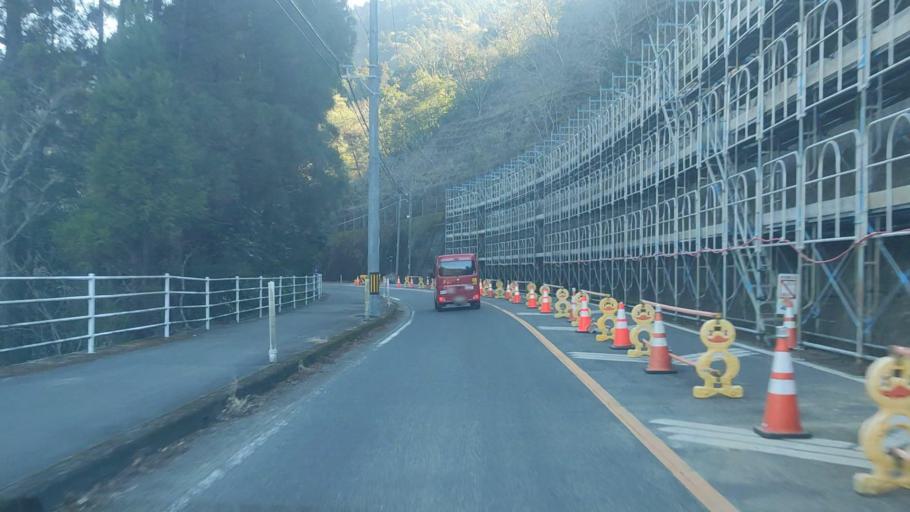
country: JP
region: Oita
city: Saiki
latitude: 32.7657
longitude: 131.7991
